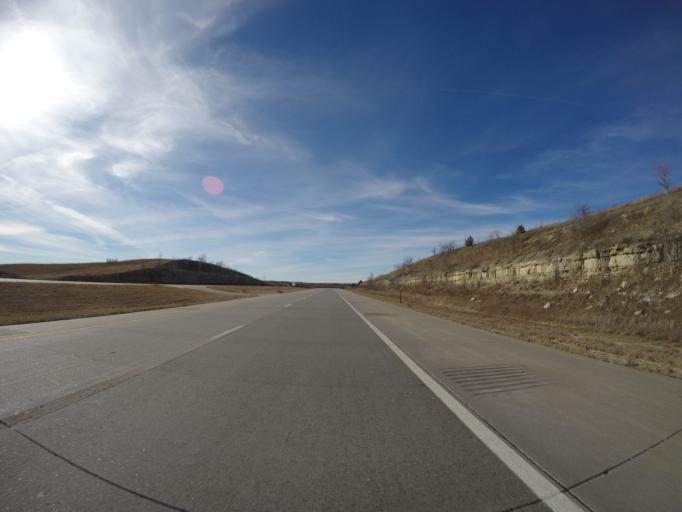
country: US
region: Kansas
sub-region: Riley County
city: Ogden
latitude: 39.0659
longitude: -96.6065
